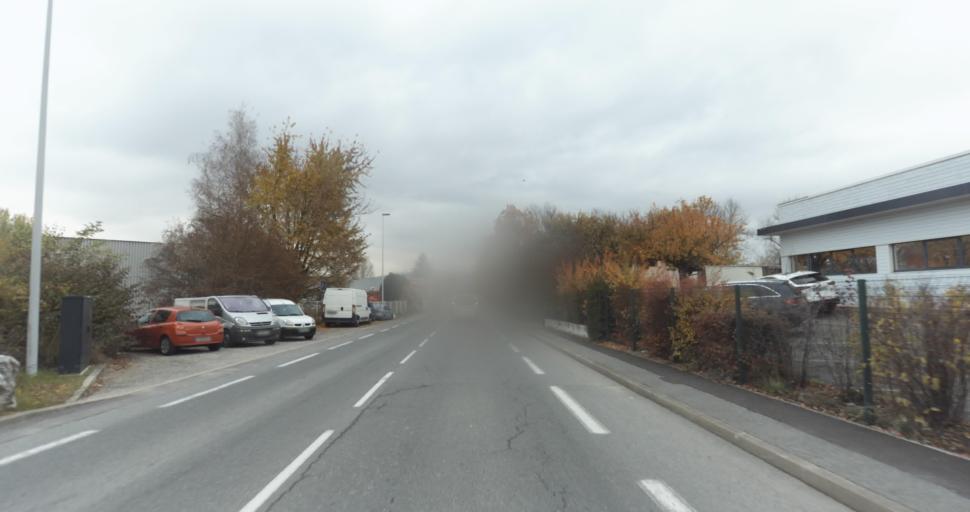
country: FR
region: Rhone-Alpes
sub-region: Departement de la Haute-Savoie
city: Pringy
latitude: 45.9426
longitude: 6.1280
